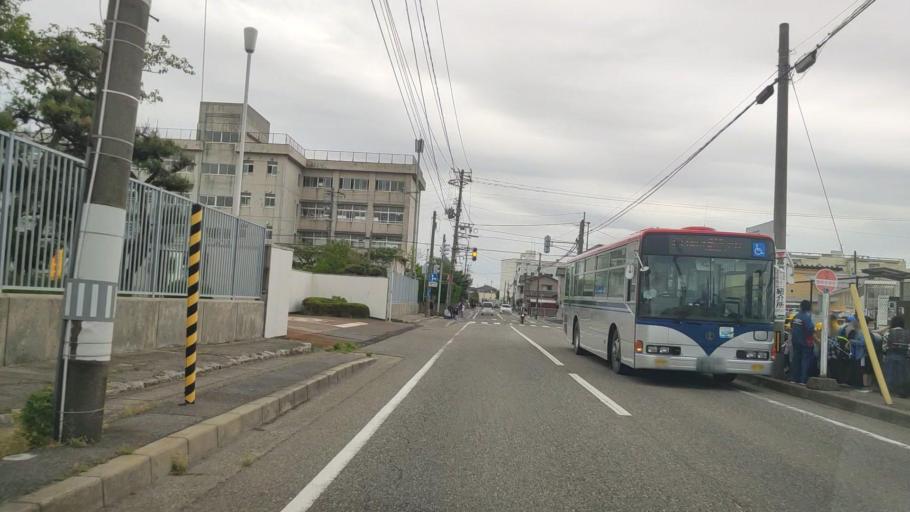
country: JP
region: Niigata
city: Niigata-shi
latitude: 37.9451
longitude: 139.0775
